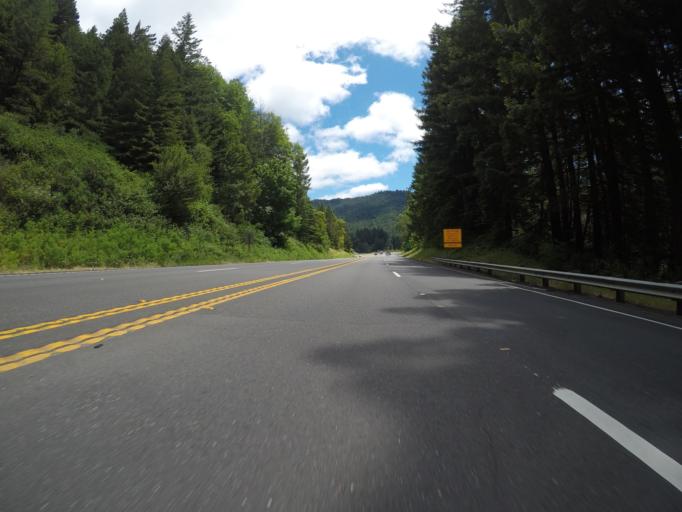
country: US
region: California
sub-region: Humboldt County
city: Redway
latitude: 40.2705
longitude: -123.8748
